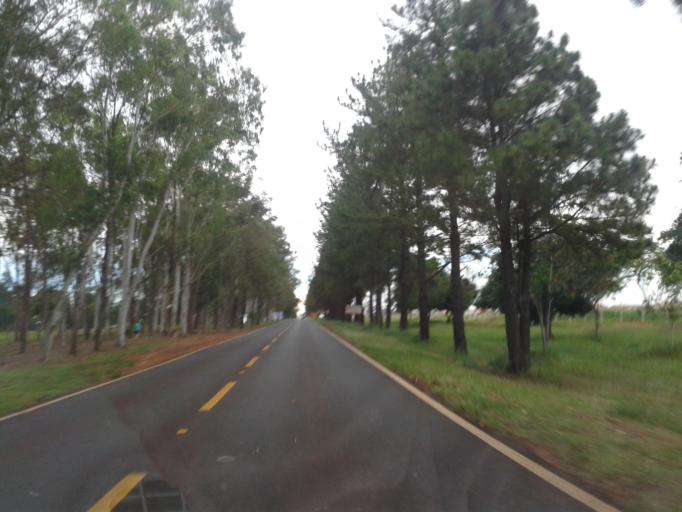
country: BR
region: Minas Gerais
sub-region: Santa Vitoria
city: Santa Vitoria
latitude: -18.8676
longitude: -50.1252
